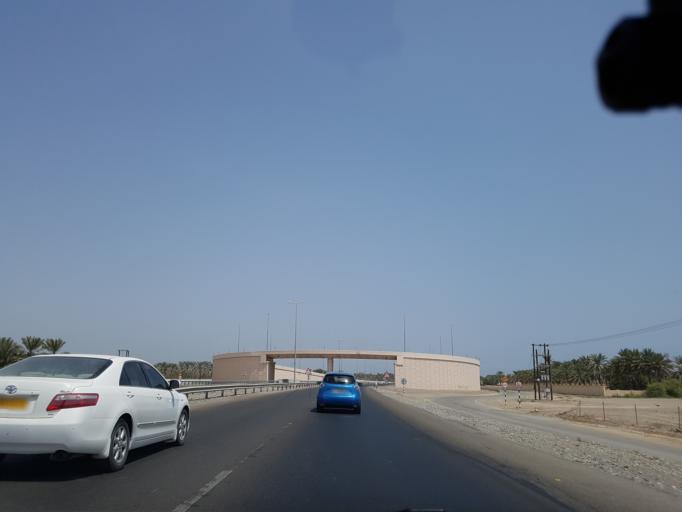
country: OM
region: Al Batinah
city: Saham
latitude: 24.1790
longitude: 56.8569
